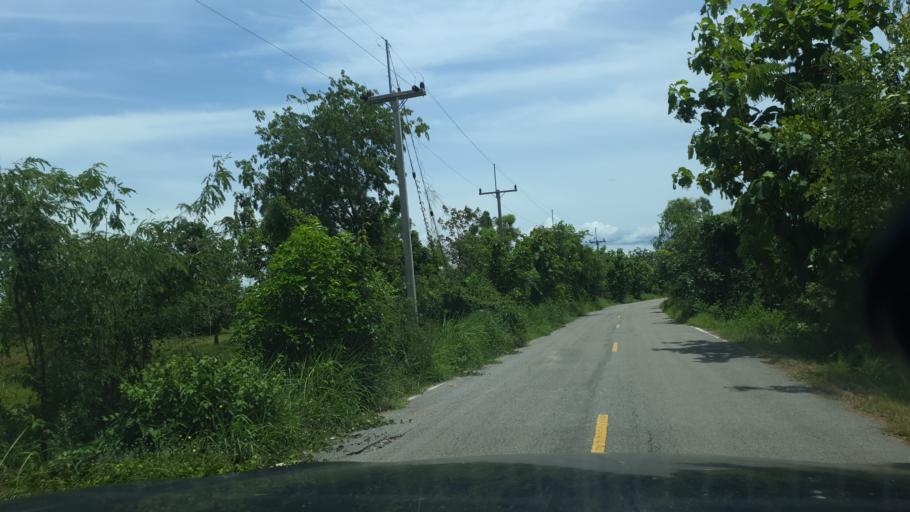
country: TH
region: Sukhothai
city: Ban Na
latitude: 17.1244
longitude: 99.6734
